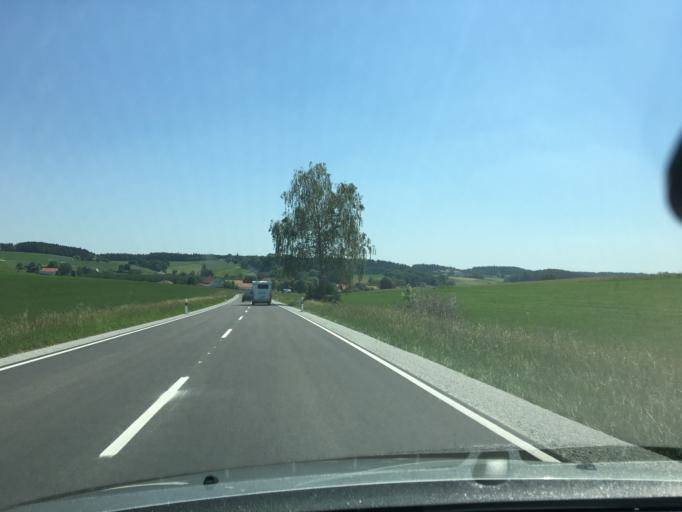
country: DE
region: Bavaria
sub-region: Upper Bavaria
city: Niedertaufkirchen
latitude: 48.3196
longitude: 12.5489
